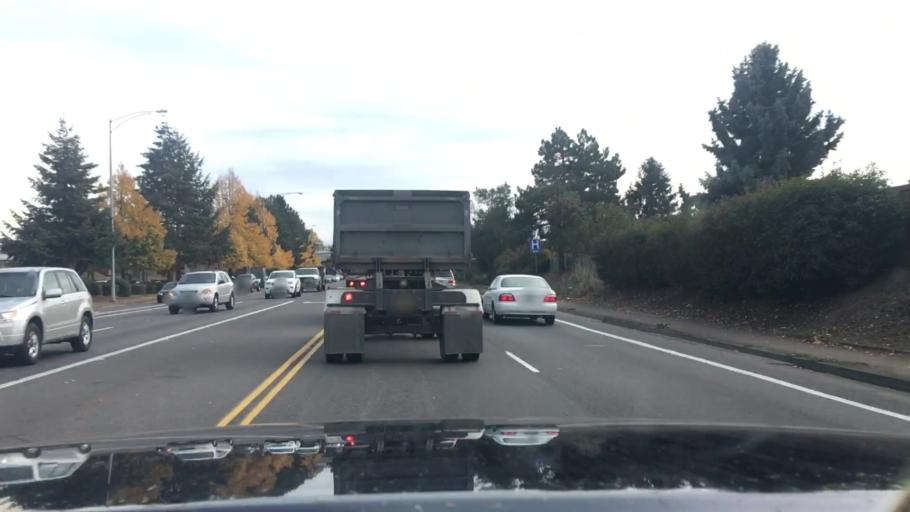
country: US
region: Oregon
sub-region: Lane County
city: Eugene
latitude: 44.0900
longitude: -123.0678
